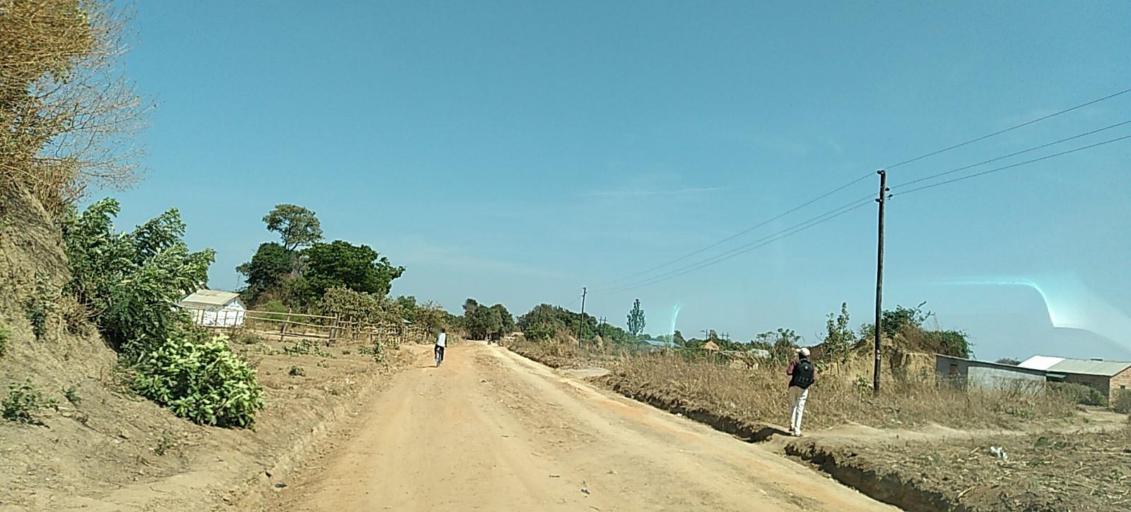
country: ZM
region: Copperbelt
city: Chililabombwe
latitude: -12.3349
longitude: 27.8619
